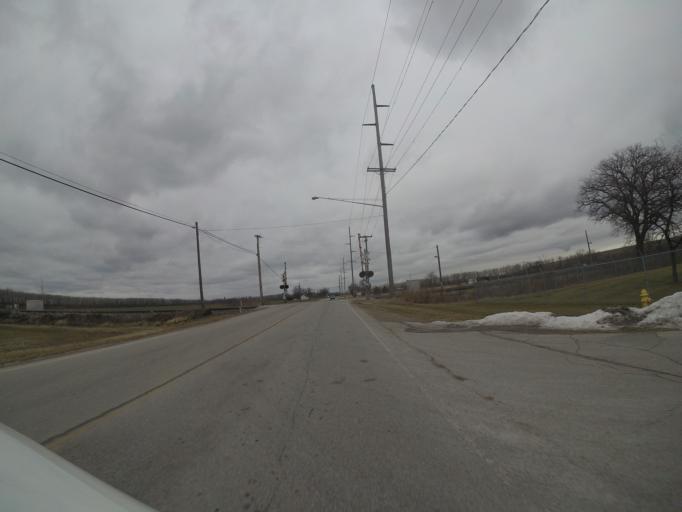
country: US
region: Ohio
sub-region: Wood County
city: Walbridge
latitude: 41.5948
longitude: -83.5127
